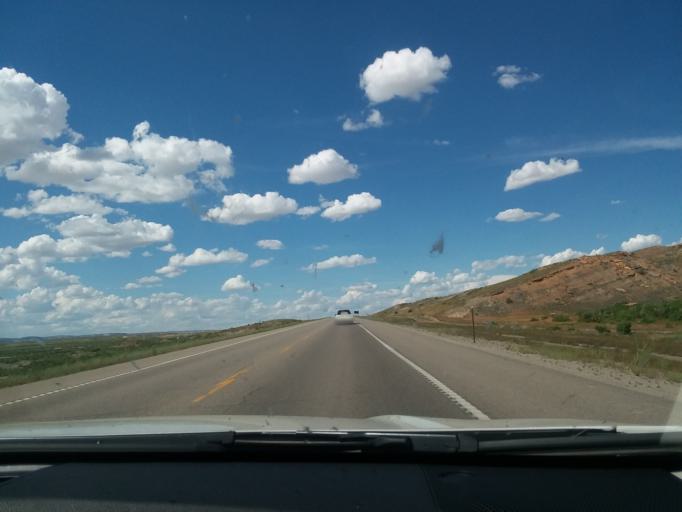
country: US
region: Wyoming
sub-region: Sweetwater County
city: North Rock Springs
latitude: 41.6401
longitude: -109.2290
